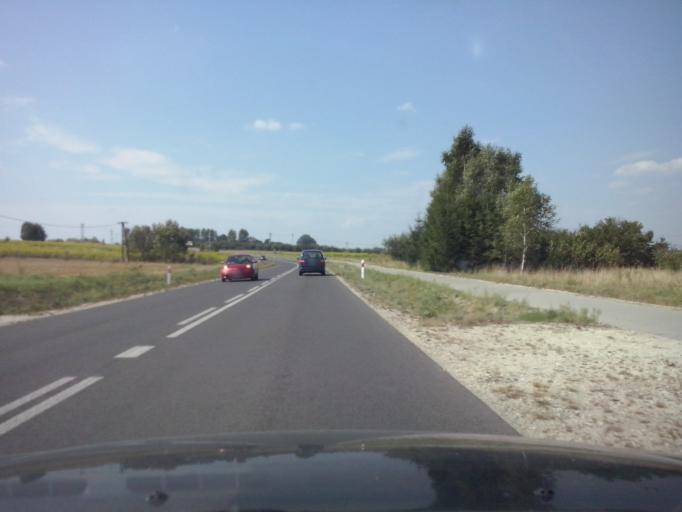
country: PL
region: Swietokrzyskie
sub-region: Powiat kielecki
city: Chmielnik
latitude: 50.6165
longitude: 20.7717
